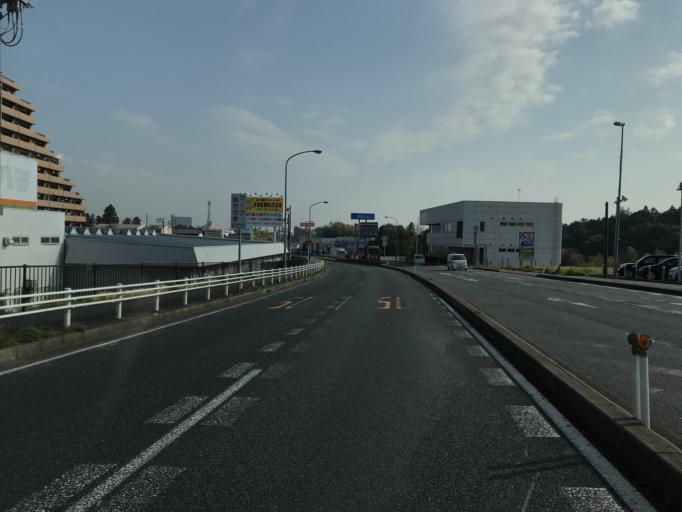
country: JP
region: Chiba
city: Narita
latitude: 35.7627
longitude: 140.3073
